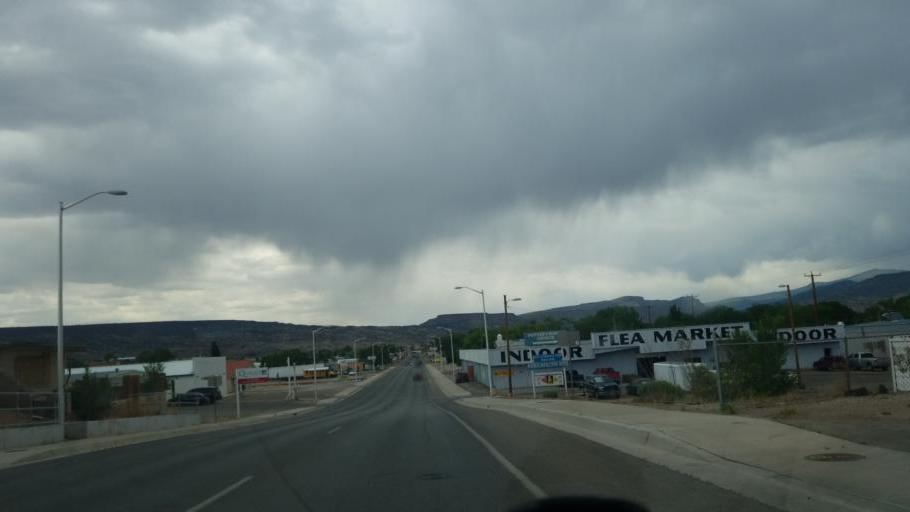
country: US
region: New Mexico
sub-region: Cibola County
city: Grants
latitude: 35.1527
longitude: -107.8476
